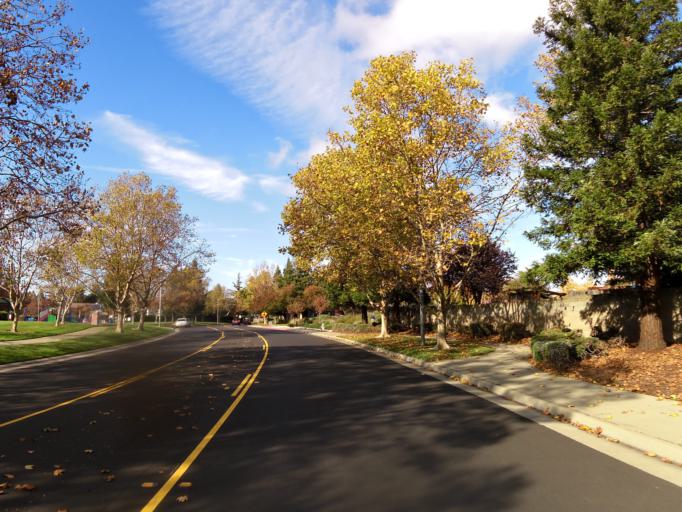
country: US
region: California
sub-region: Sacramento County
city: Elk Grove
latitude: 38.4157
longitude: -121.3948
